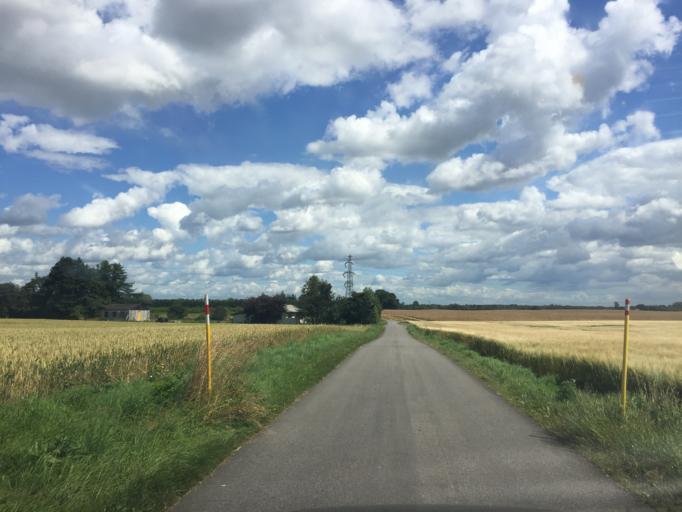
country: DK
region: Capital Region
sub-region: Hoje-Taastrup Kommune
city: Taastrup
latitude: 55.6956
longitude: 12.2608
